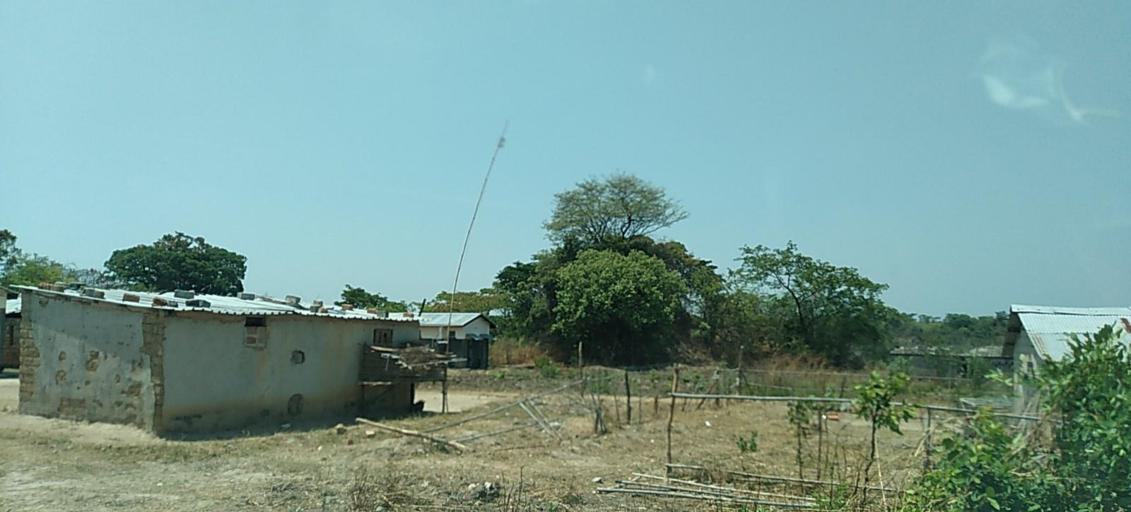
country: ZM
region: Copperbelt
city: Luanshya
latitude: -12.9936
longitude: 28.3263
